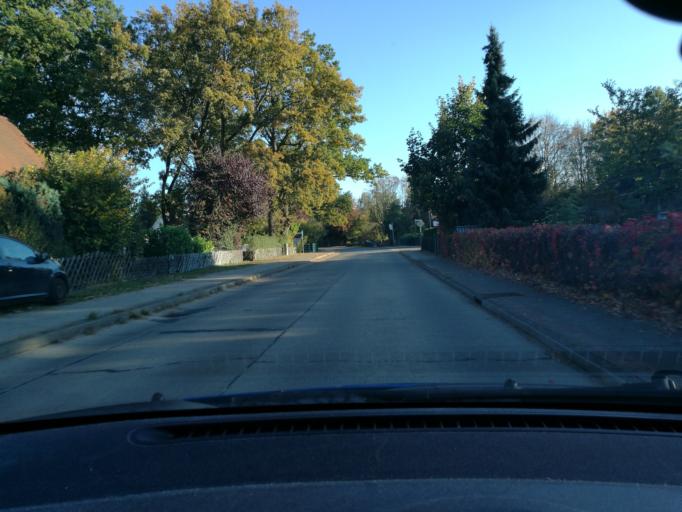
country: DE
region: Lower Saxony
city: Bleckede
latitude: 53.2825
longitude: 10.7542
